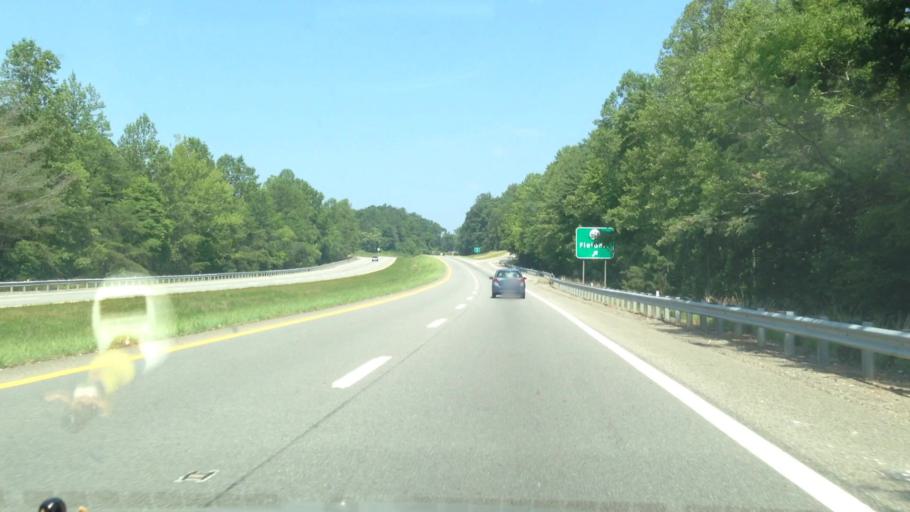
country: US
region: Virginia
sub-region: Henry County
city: Collinsville
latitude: 36.6914
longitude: -79.9466
